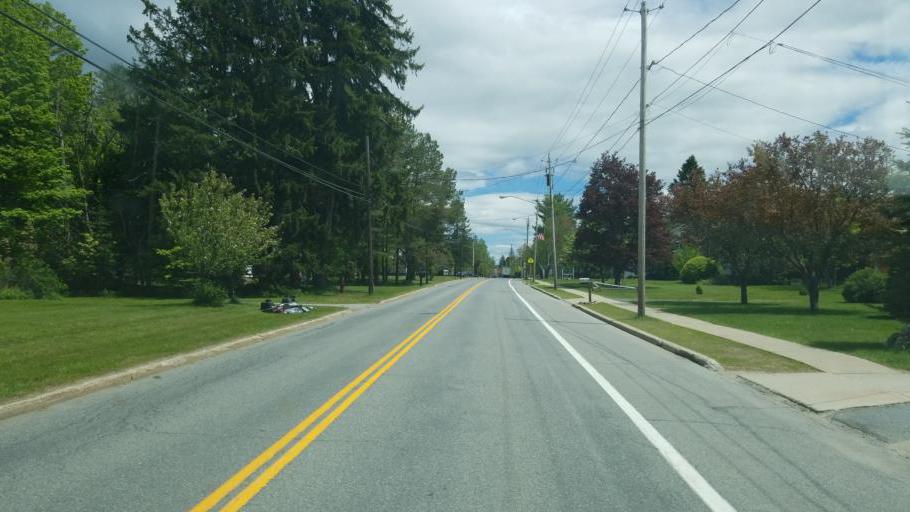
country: US
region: New York
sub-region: Hamilton County
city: Lake Pleasant
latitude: 43.7831
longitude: -74.2743
